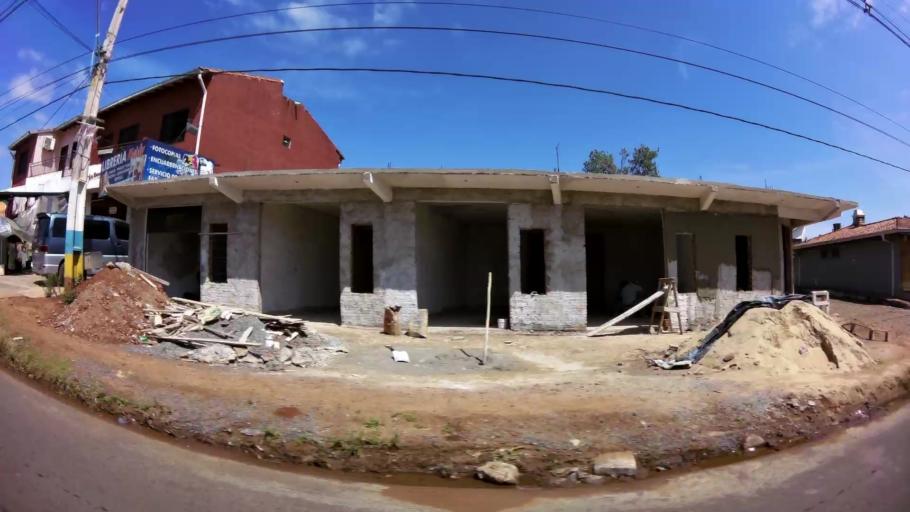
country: PY
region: Central
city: San Lorenzo
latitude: -25.3089
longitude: -57.5057
